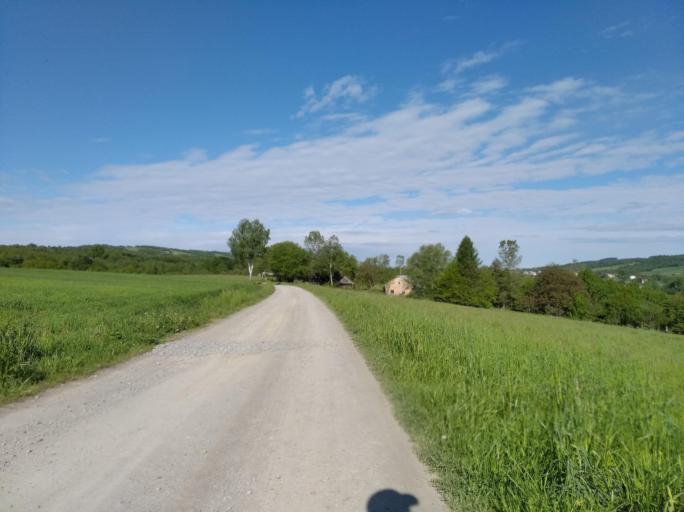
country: PL
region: Subcarpathian Voivodeship
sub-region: Powiat strzyzowski
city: Frysztak
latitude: 49.8404
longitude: 21.5724
